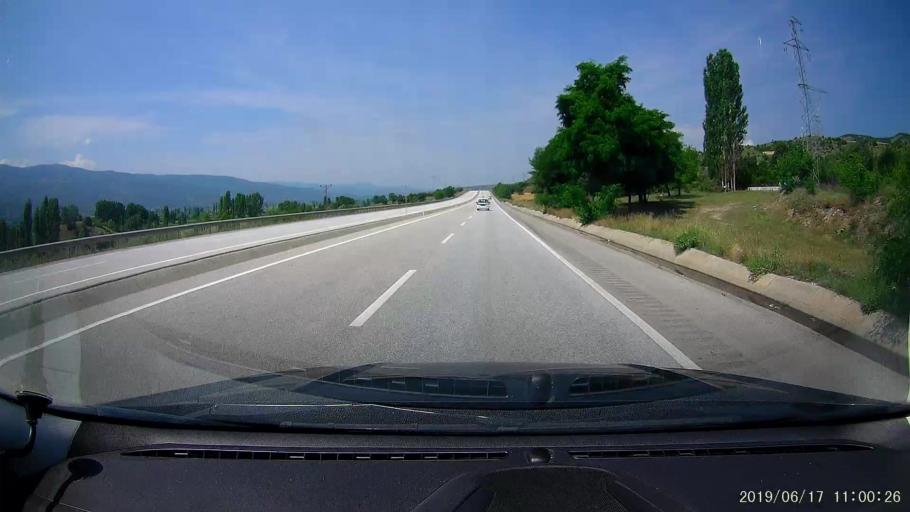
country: TR
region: Kastamonu
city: Tosya
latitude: 41.0345
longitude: 34.1805
